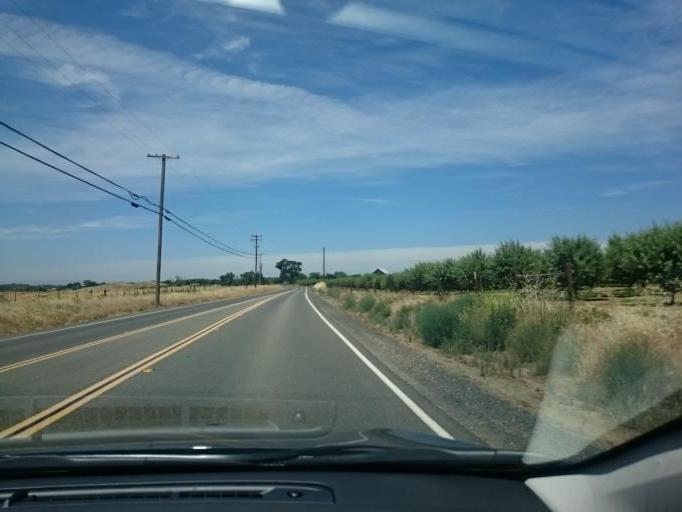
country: US
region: California
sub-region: Stanislaus County
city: Waterford
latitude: 37.6462
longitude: -120.6898
